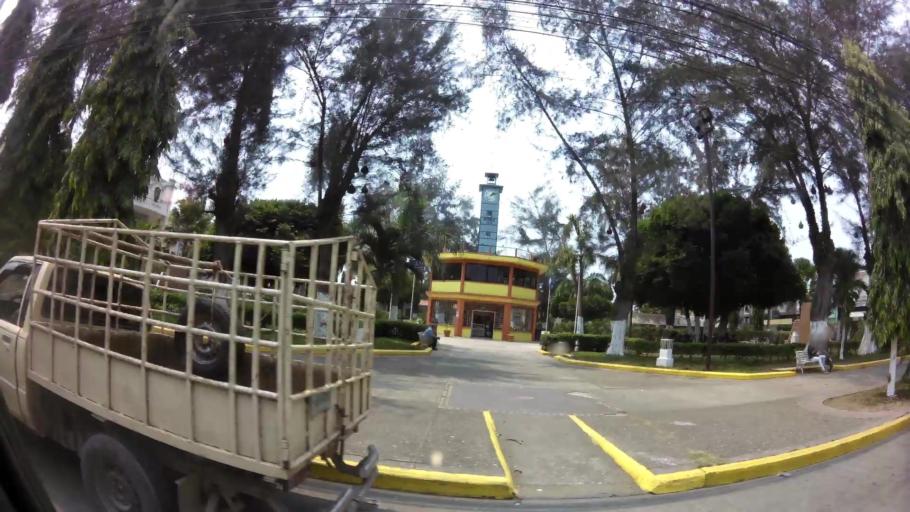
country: HN
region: Yoro
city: El Progreso
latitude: 15.4006
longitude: -87.8120
